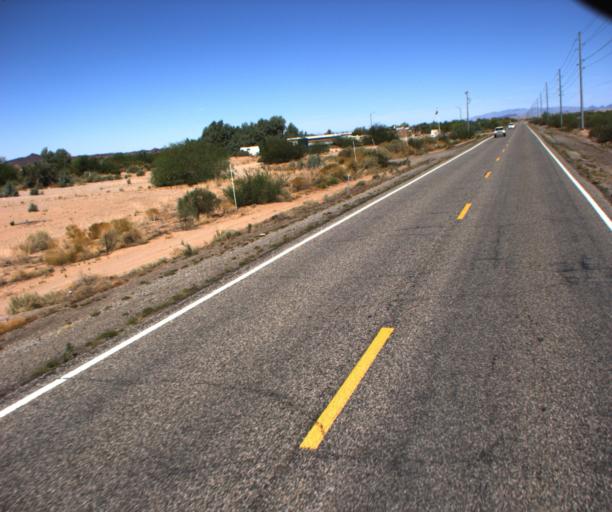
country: US
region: Arizona
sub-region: La Paz County
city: Cienega Springs
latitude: 33.9463
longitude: -114.0165
